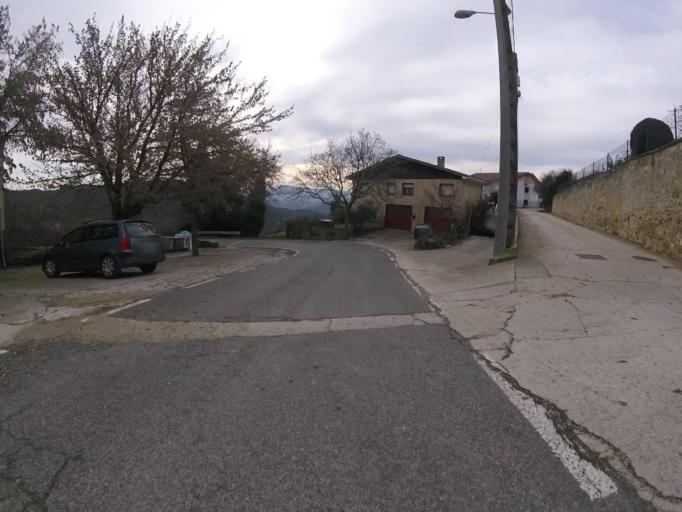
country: ES
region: Navarre
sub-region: Provincia de Navarra
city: Estella
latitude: 42.7167
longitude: -2.0506
